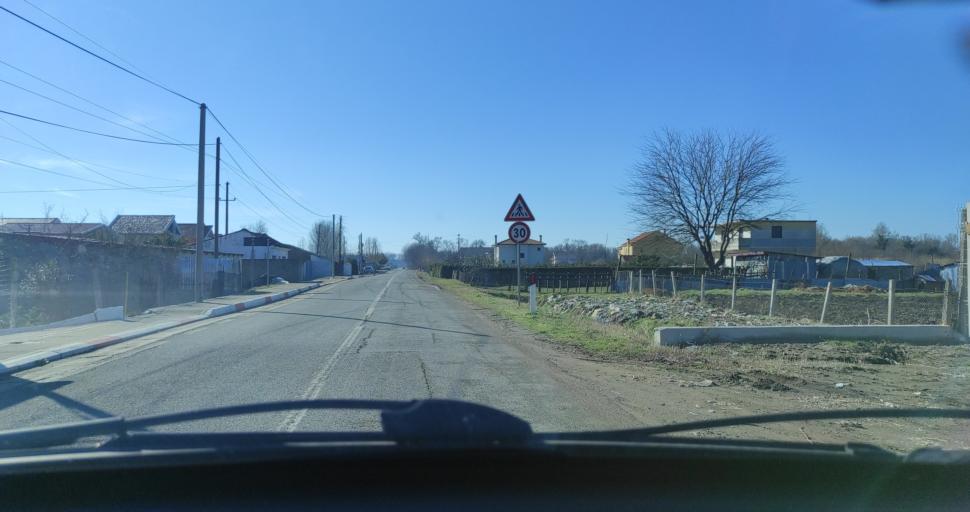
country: AL
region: Shkoder
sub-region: Rrethi i Shkodres
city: Velipoje
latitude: 41.8788
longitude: 19.4038
